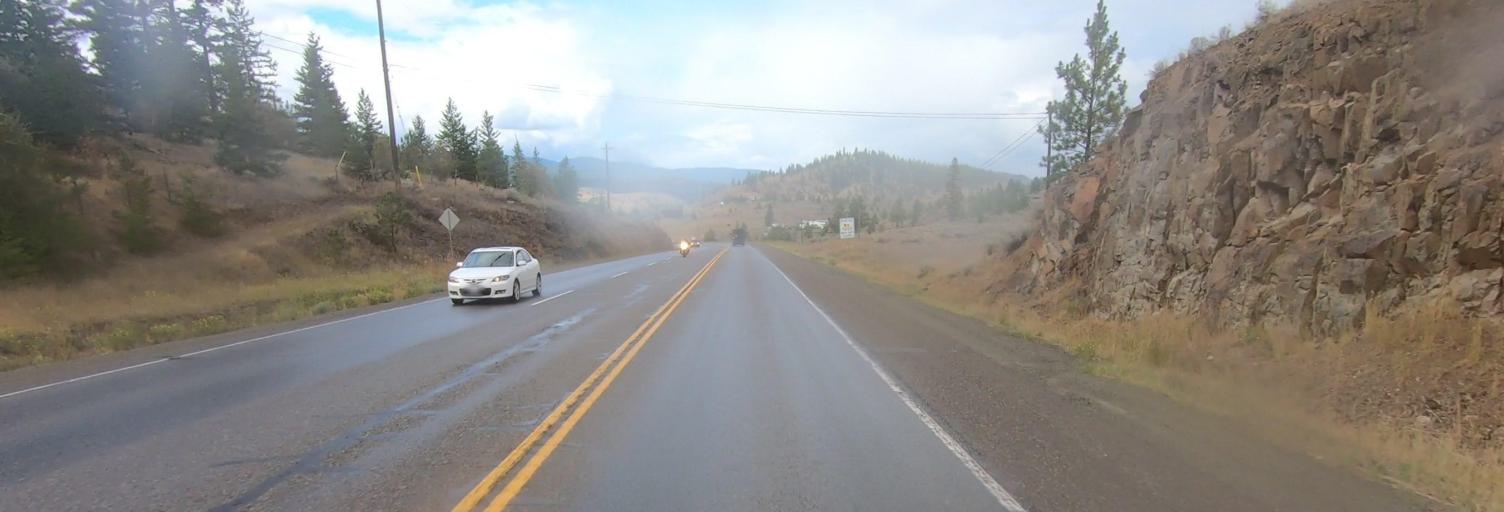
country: CA
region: British Columbia
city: Kamloops
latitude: 50.6612
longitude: -120.5378
